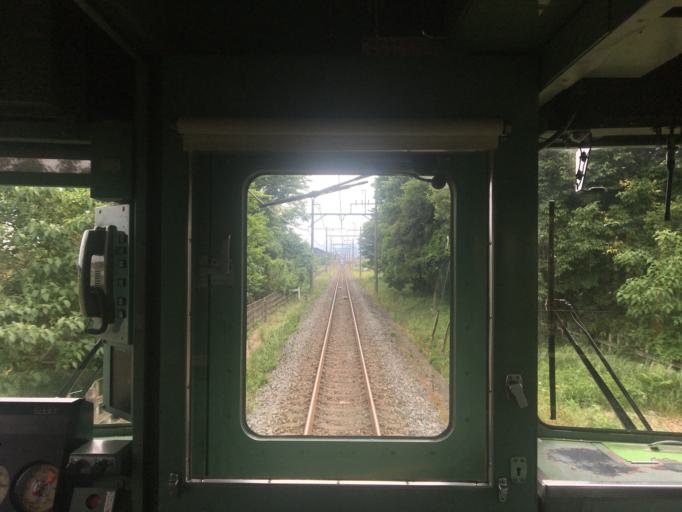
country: JP
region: Saitama
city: Sakado
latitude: 35.9465
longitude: 139.3786
